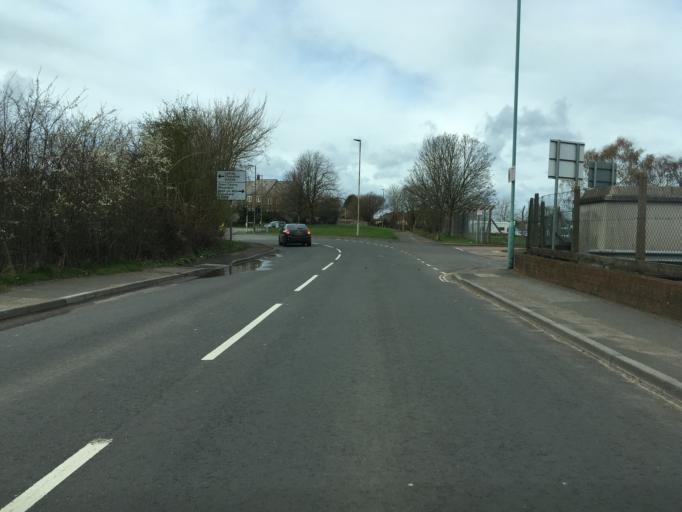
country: GB
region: England
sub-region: Gloucestershire
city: Coleford
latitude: 51.7864
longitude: -2.6127
